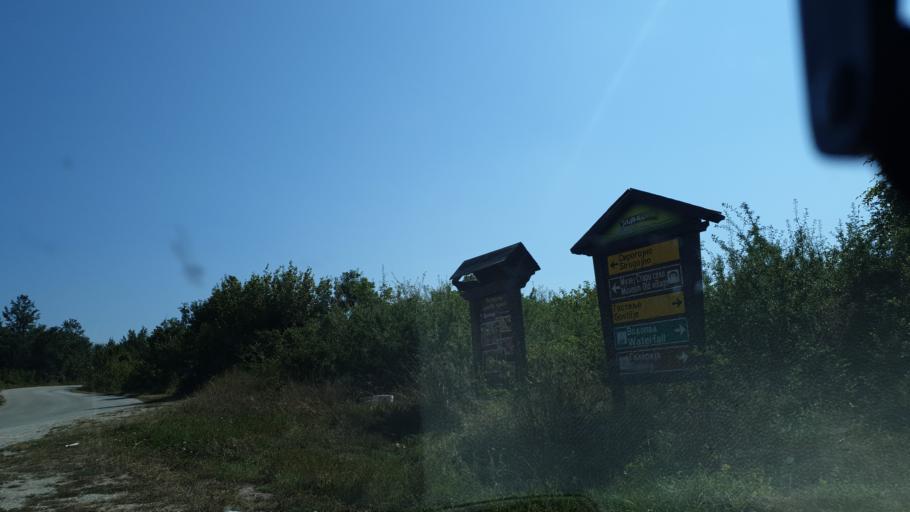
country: RS
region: Central Serbia
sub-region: Zlatiborski Okrug
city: Cajetina
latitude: 43.6987
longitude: 19.8547
